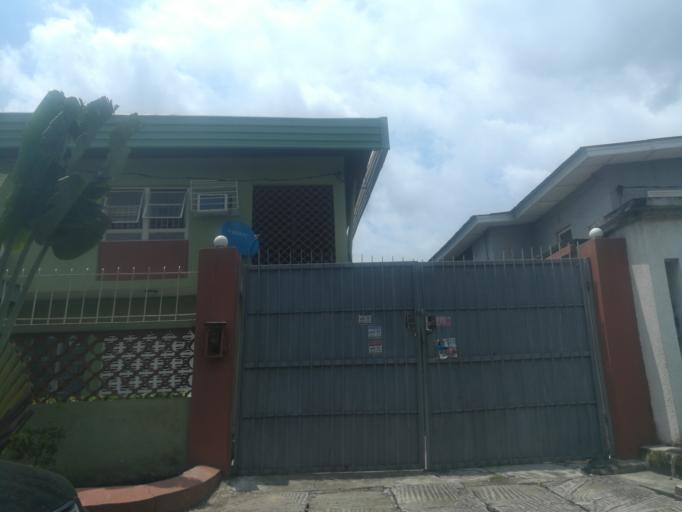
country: NG
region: Lagos
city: Ojota
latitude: 6.5617
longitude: 3.3937
